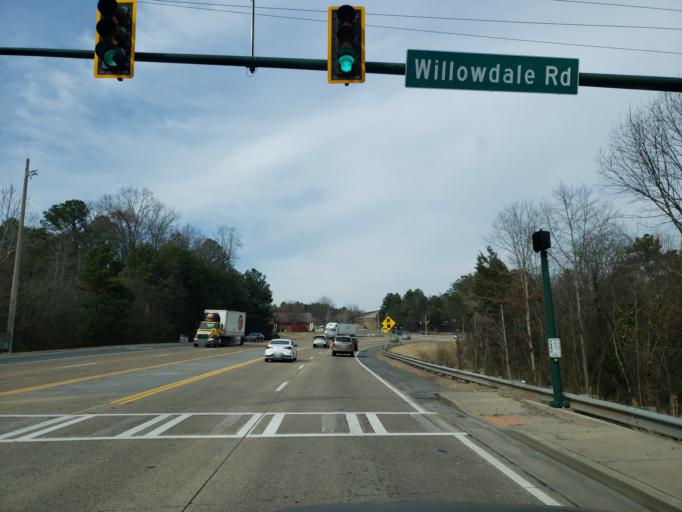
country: US
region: Georgia
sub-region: Whitfield County
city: Dalton
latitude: 34.7987
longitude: -84.9935
